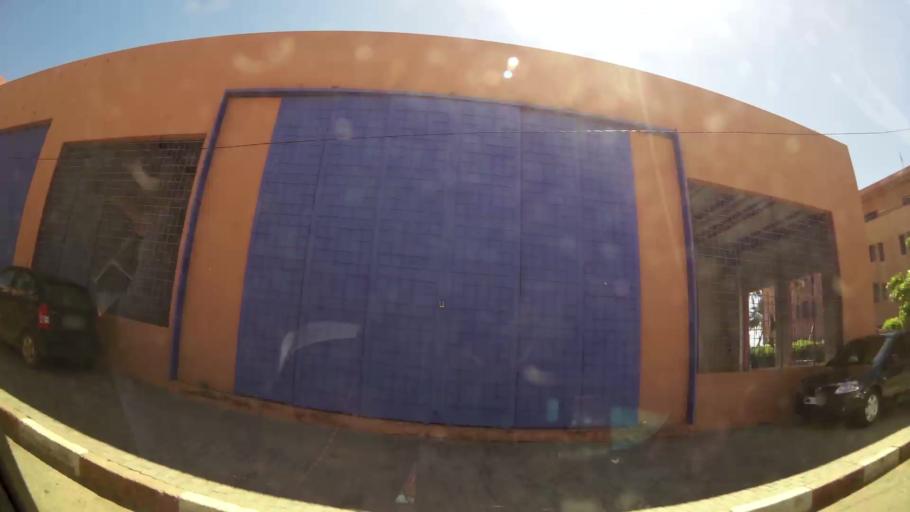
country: MA
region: Marrakech-Tensift-Al Haouz
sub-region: Marrakech
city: Marrakesh
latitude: 31.6475
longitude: -7.9877
